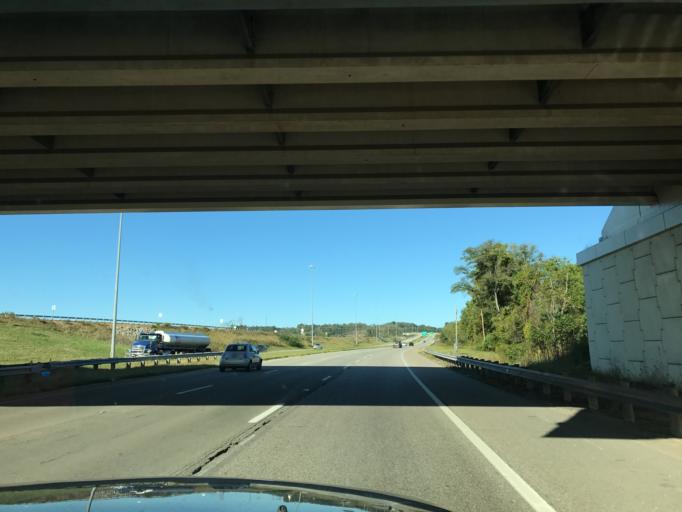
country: US
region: West Virginia
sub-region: Wood County
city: Blennerhassett
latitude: 39.2847
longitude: -81.6466
